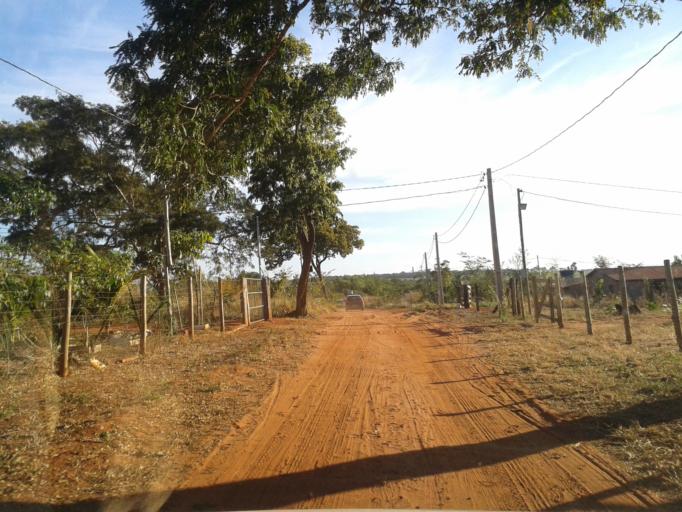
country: BR
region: Minas Gerais
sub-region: Santa Vitoria
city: Santa Vitoria
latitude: -18.9983
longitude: -50.3801
